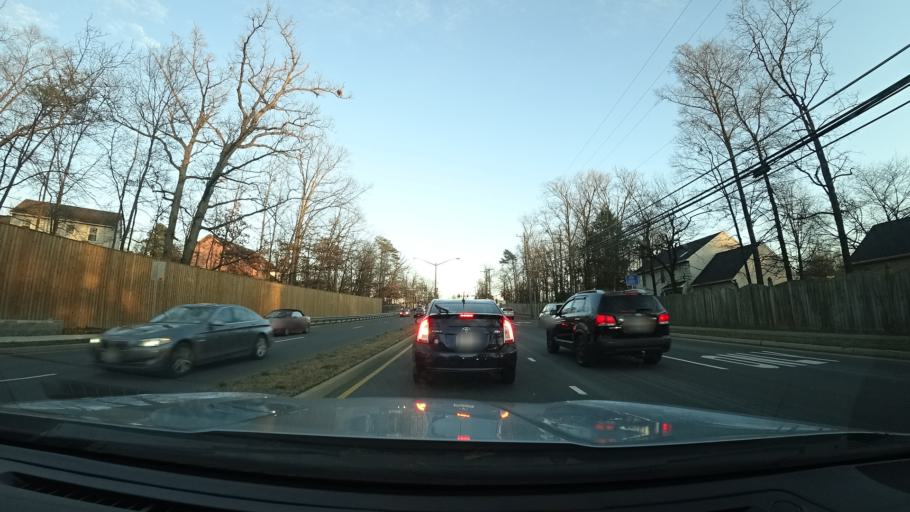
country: US
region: Virginia
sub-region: Loudoun County
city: Oak Grove
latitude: 38.9755
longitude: -77.4059
